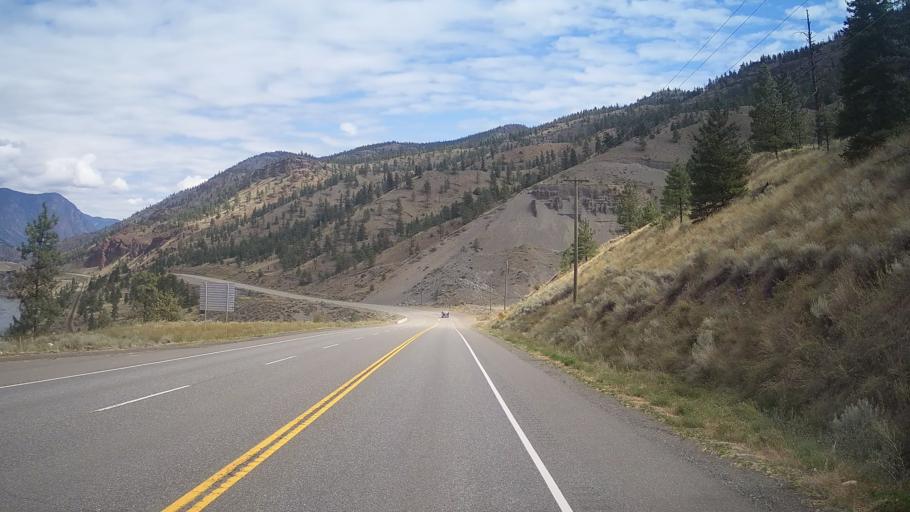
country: CA
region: British Columbia
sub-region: Thompson-Nicola Regional District
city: Ashcroft
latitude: 50.2928
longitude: -121.3946
